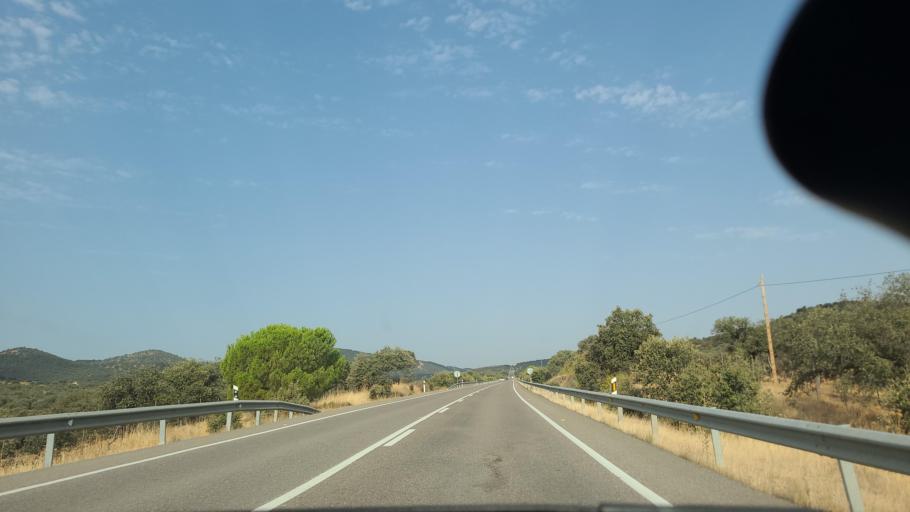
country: ES
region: Andalusia
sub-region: Province of Cordoba
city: Espiel
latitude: 38.1852
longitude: -5.0625
